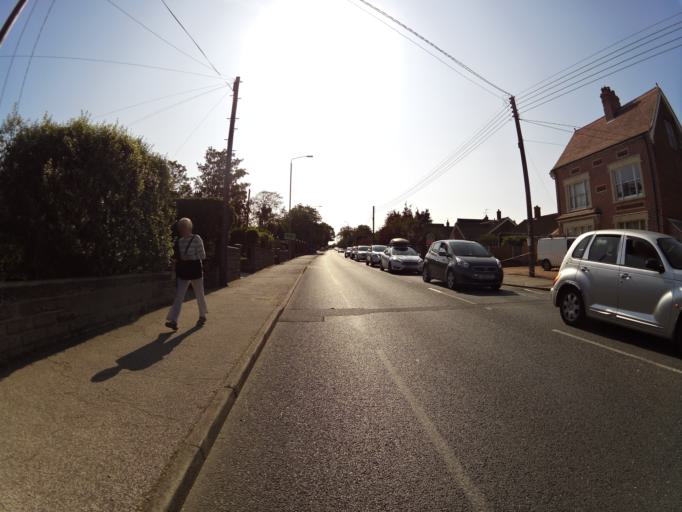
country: GB
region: England
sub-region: Suffolk
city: Lowestoft
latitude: 52.4679
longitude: 1.7076
